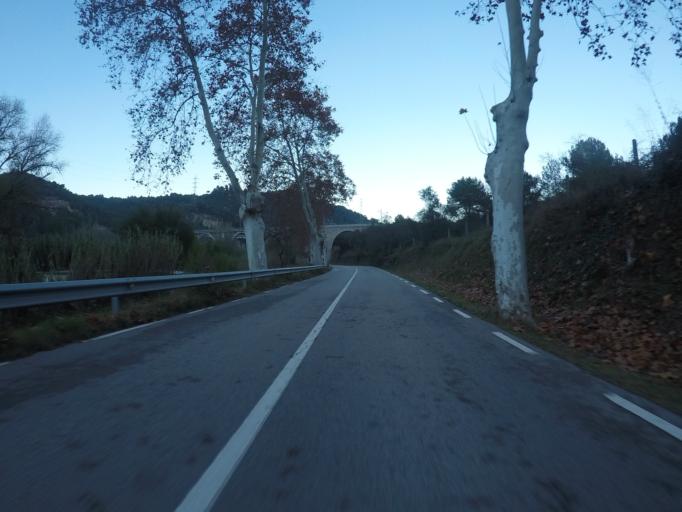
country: ES
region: Catalonia
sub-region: Provincia de Barcelona
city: Monistrol de Montserrat
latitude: 41.6200
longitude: 1.8536
